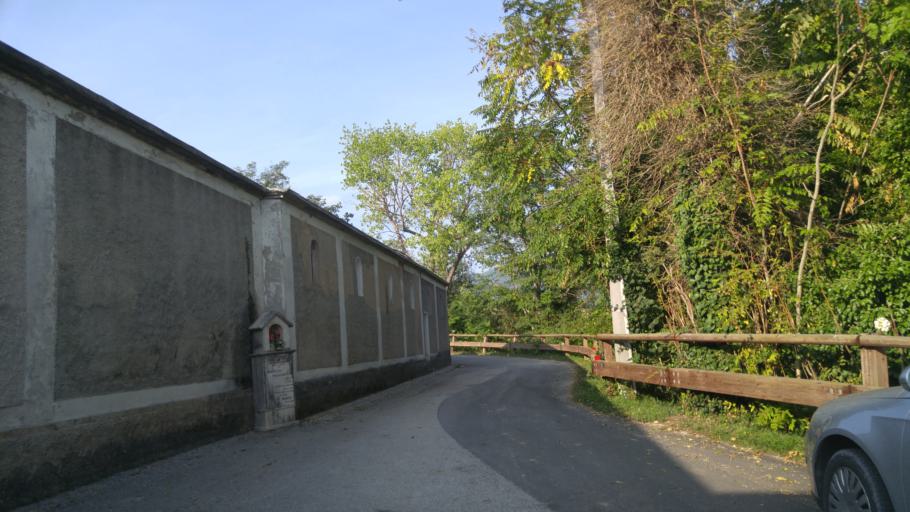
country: IT
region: The Marches
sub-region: Provincia di Pesaro e Urbino
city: Acqualagna
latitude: 43.6207
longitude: 12.6705
